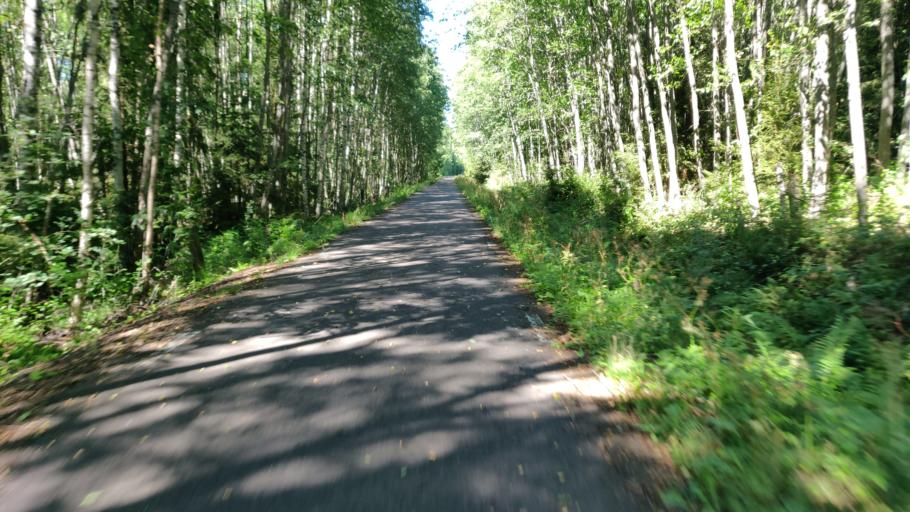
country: SE
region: Vaermland
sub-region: Hagfors Kommun
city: Hagfors
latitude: 59.9583
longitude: 13.5731
